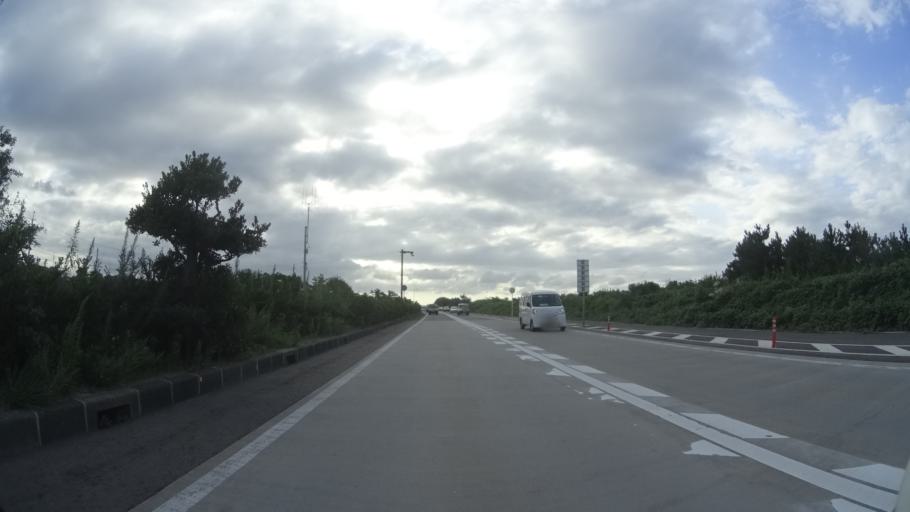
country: JP
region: Tottori
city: Kurayoshi
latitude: 35.4984
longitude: 133.7902
